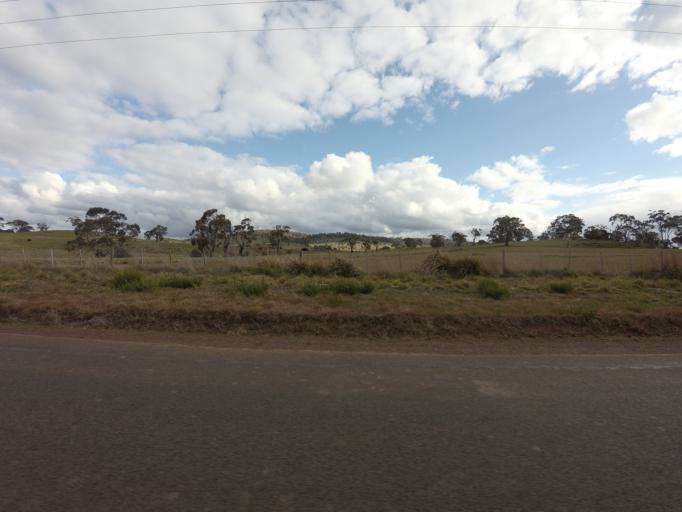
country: AU
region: Tasmania
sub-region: Northern Midlands
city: Evandale
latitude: -41.8868
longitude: 147.3153
